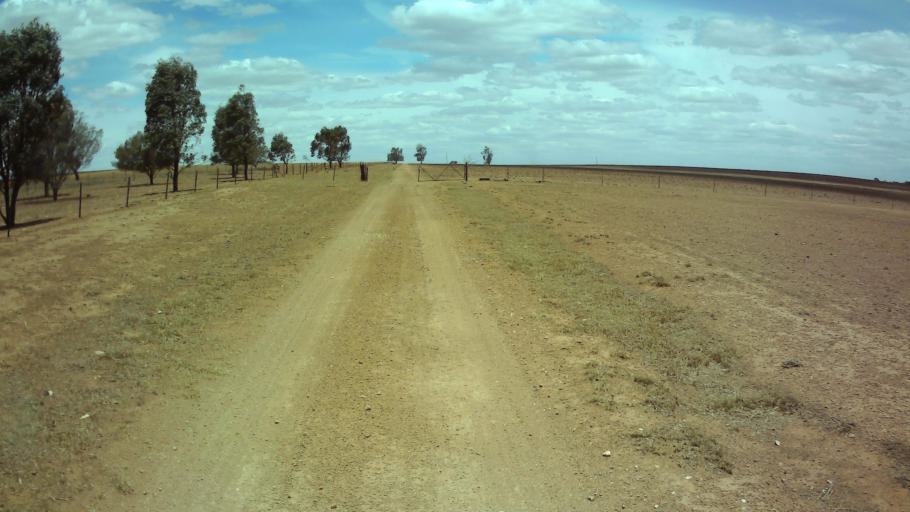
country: AU
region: New South Wales
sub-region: Weddin
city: Grenfell
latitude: -33.8965
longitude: 147.7402
